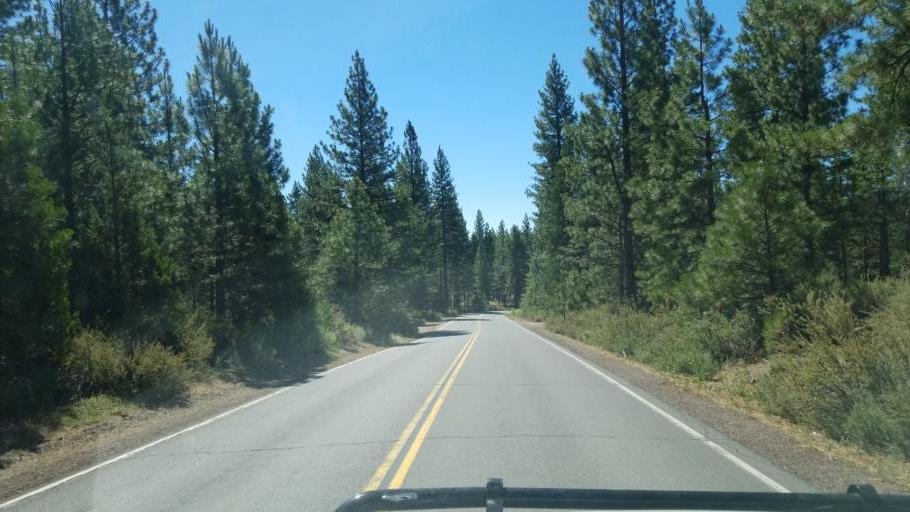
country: US
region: California
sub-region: Lassen County
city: Susanville
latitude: 40.4292
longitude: -120.7287
